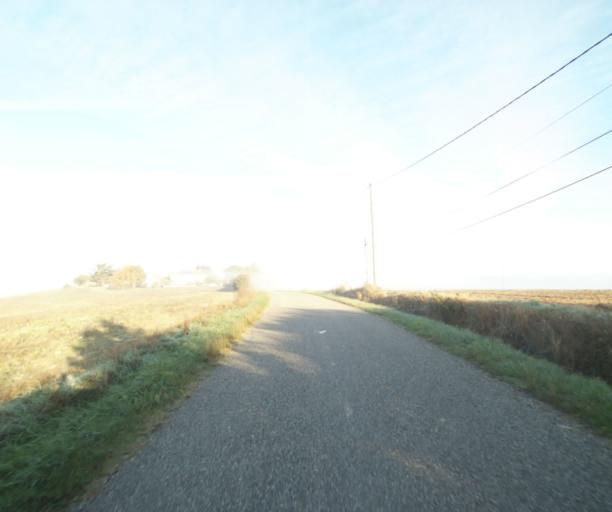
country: FR
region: Midi-Pyrenees
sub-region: Departement de la Haute-Garonne
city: Villemur-sur-Tarn
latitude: 43.9165
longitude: 1.4946
